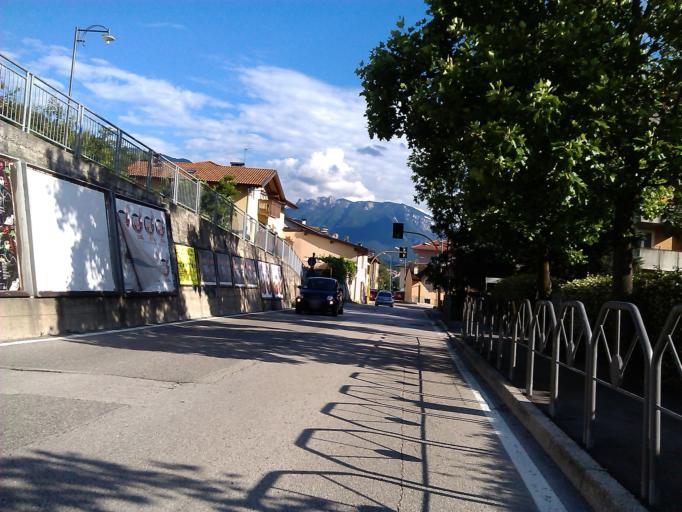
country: IT
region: Trentino-Alto Adige
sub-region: Provincia di Trento
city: Meano
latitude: 46.1009
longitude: 11.1186
